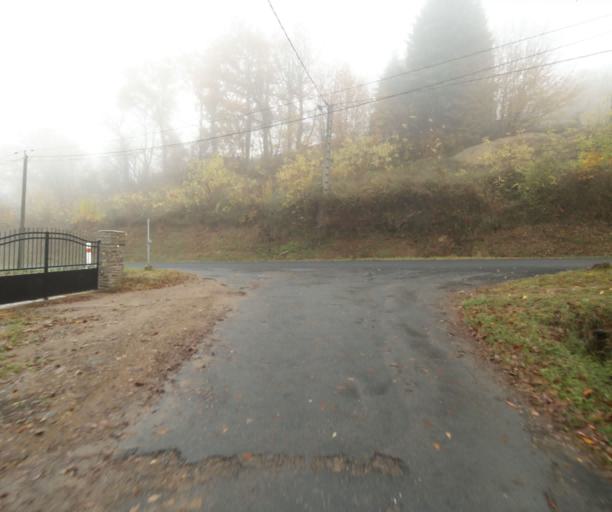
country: FR
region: Limousin
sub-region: Departement de la Correze
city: Sainte-Fereole
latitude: 45.1869
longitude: 1.6195
